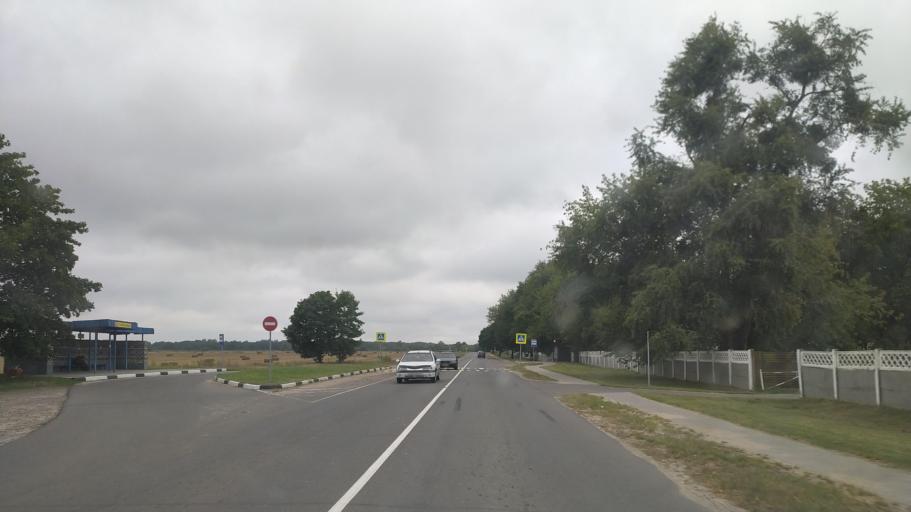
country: BY
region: Brest
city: Byaroza
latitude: 52.5541
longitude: 24.9264
